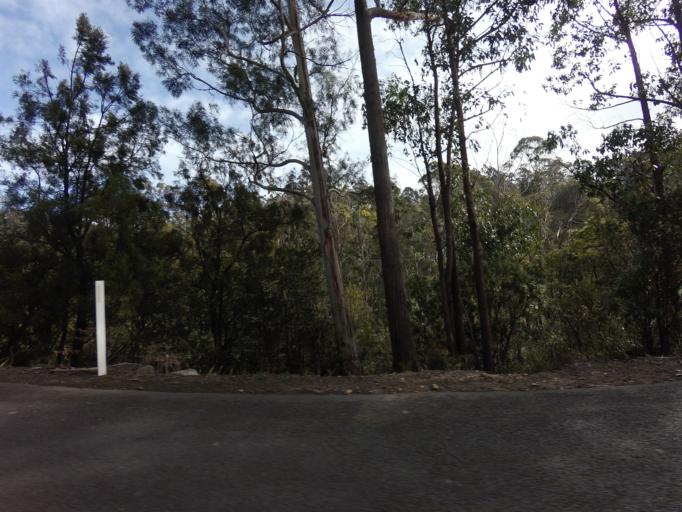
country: AU
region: Tasmania
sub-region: Kingborough
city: Margate
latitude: -43.0014
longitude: 147.1759
